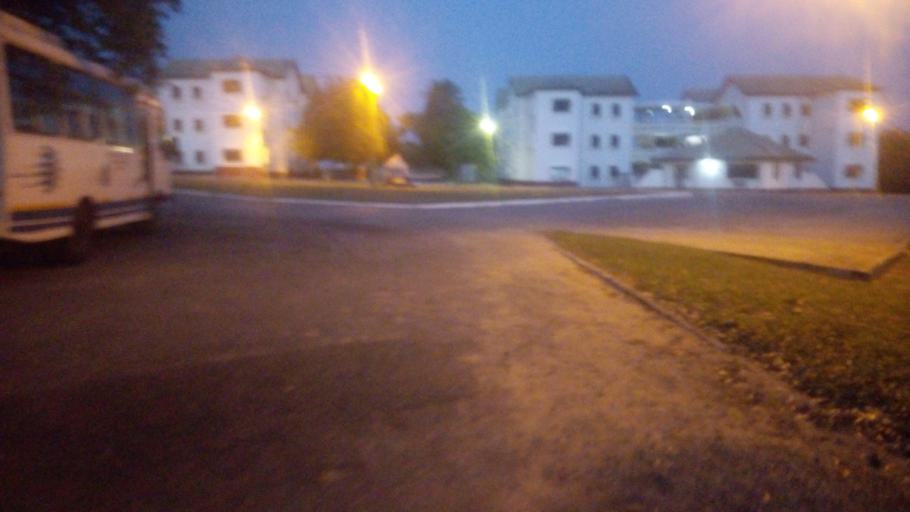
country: GH
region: Central
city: Winneba
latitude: 5.3797
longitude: -0.6255
